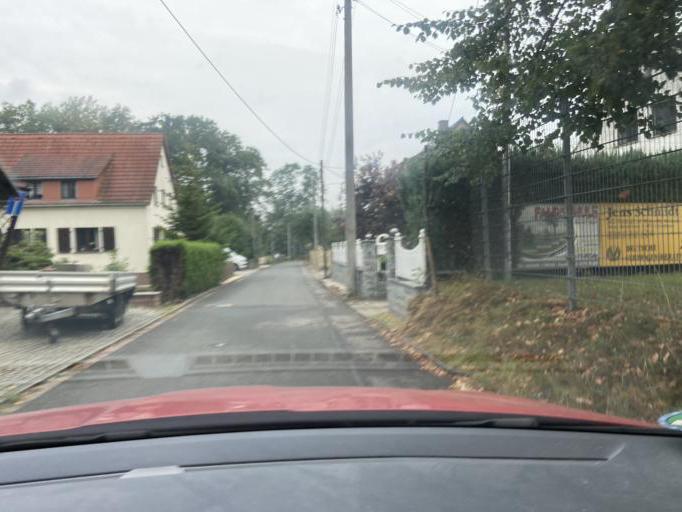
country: DE
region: Saxony
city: Wilsdruff
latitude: 51.0320
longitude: 13.5448
